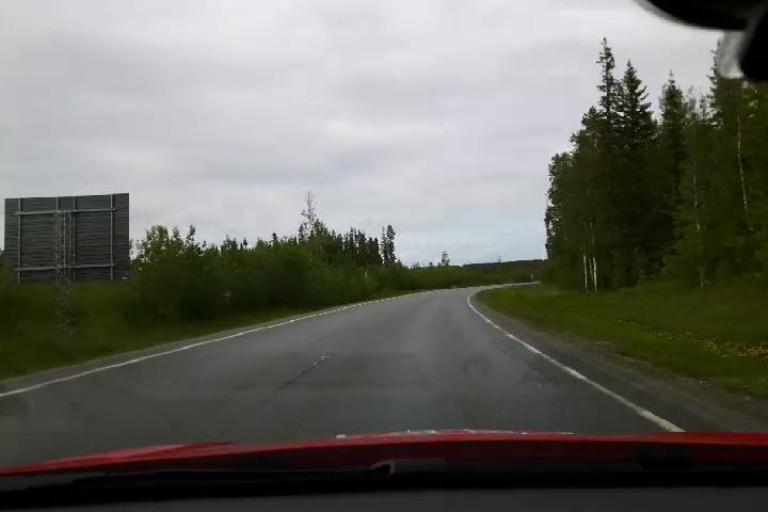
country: SE
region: Jaemtland
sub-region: Bergs Kommun
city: Hoverberg
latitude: 62.9170
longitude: 14.3282
